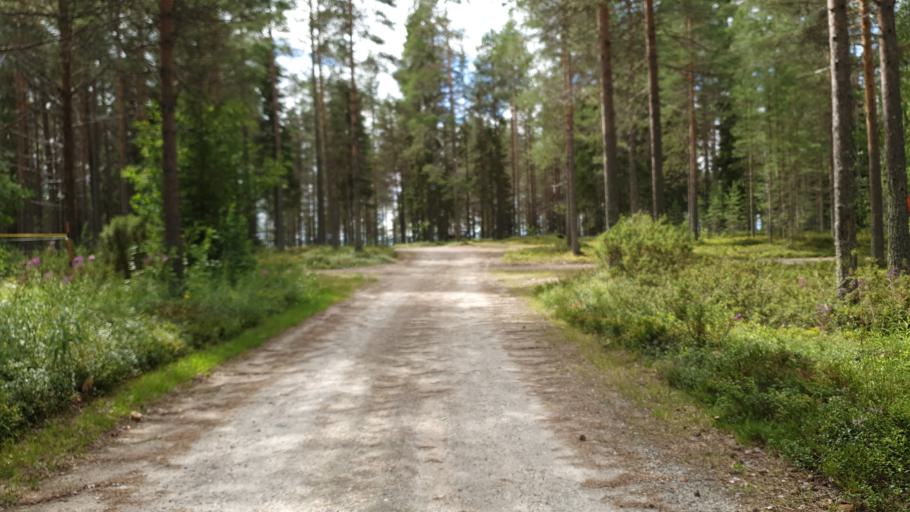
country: FI
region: Kainuu
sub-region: Kehys-Kainuu
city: Kuhmo
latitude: 64.3821
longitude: 29.8081
